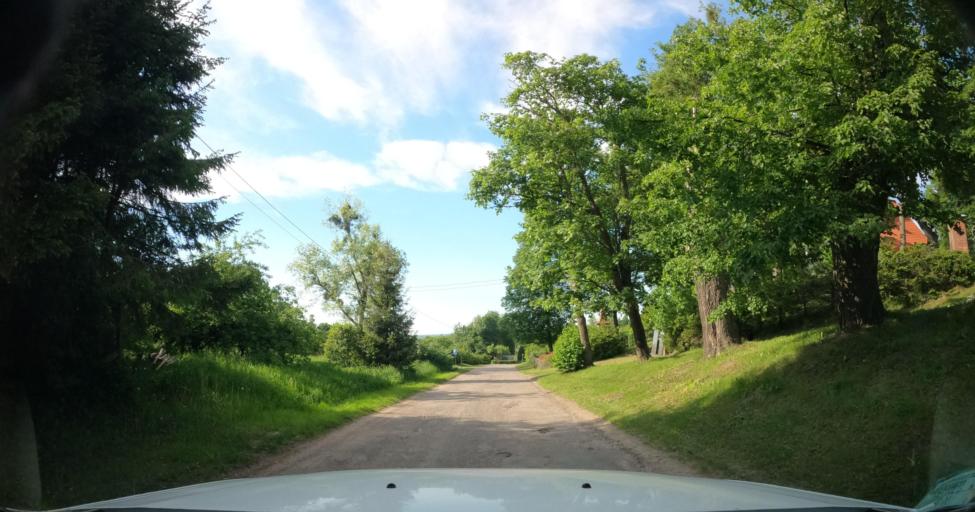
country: PL
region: Warmian-Masurian Voivodeship
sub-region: Powiat ostrodzki
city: Morag
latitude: 54.0650
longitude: 19.8892
